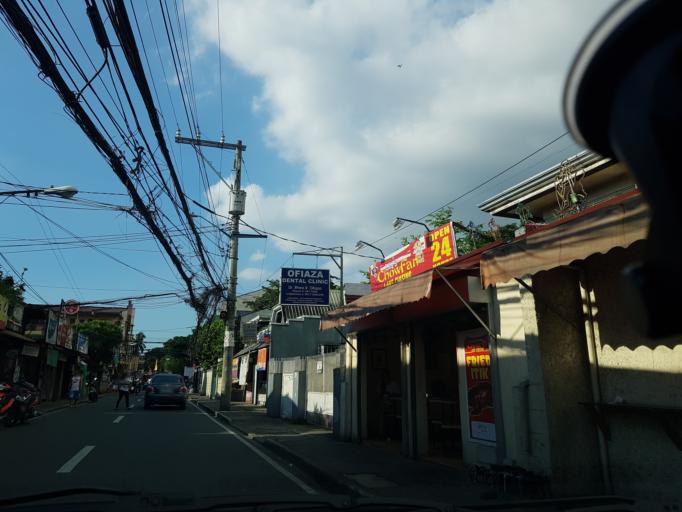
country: PH
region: Metro Manila
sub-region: Marikina
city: Calumpang
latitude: 14.6155
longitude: 121.0816
